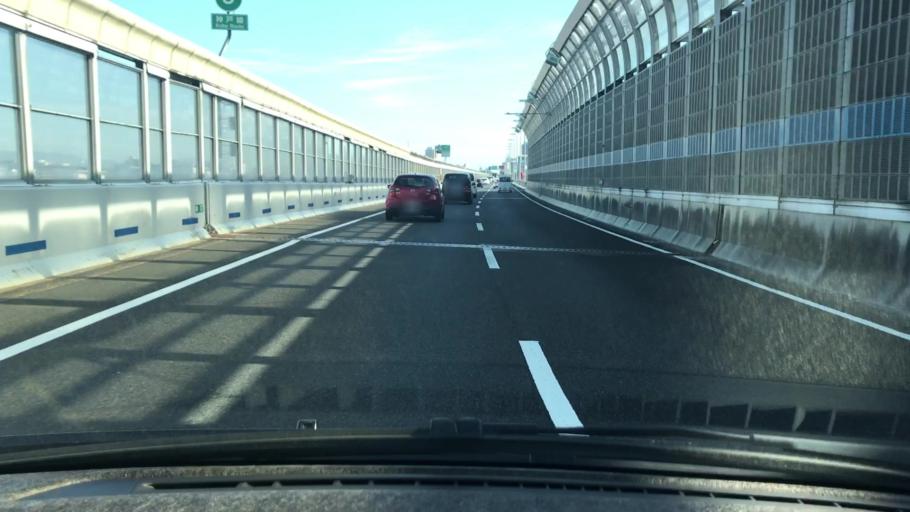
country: JP
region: Hyogo
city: Ashiya
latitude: 34.7311
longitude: 135.3175
